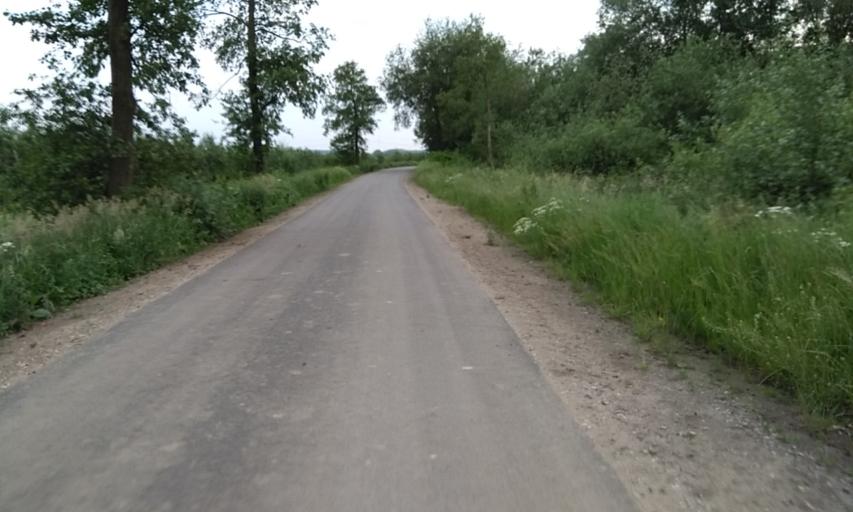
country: DE
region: Lower Saxony
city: Mittelnkirchen
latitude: 53.5160
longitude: 9.6374
